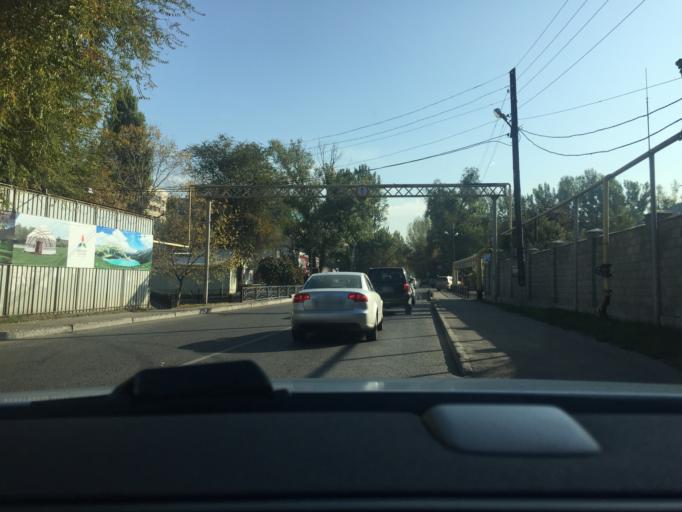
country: KZ
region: Almaty Qalasy
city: Almaty
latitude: 43.2461
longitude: 76.9177
